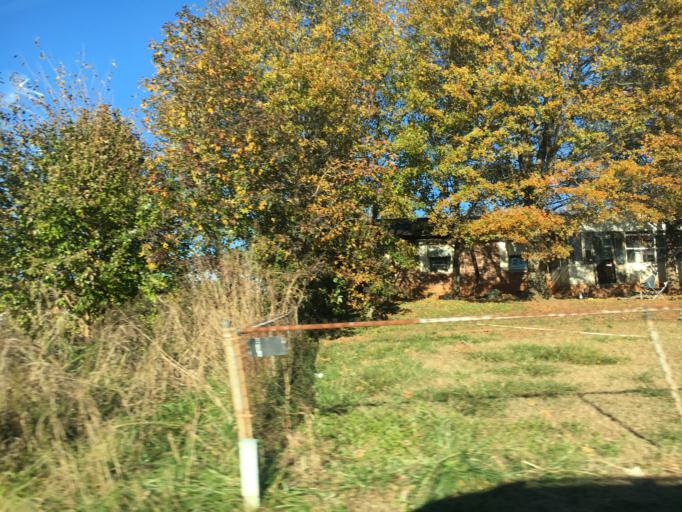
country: US
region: South Carolina
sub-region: Spartanburg County
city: Duncan
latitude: 34.9536
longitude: -82.1677
